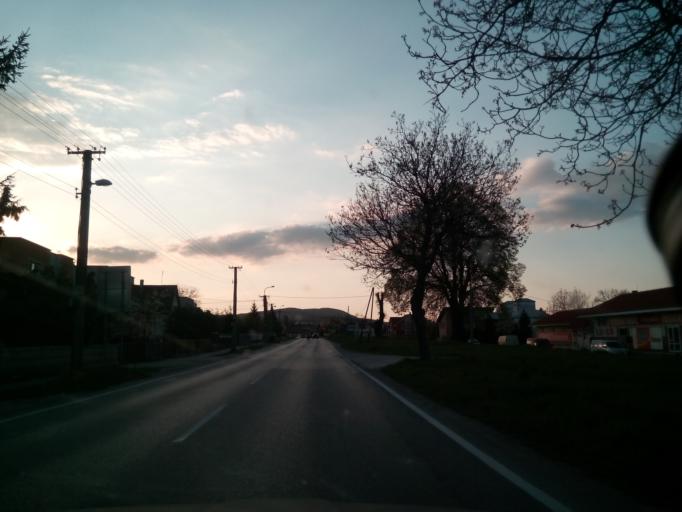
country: SK
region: Trnavsky
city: Vrbove
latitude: 48.6145
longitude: 17.7349
